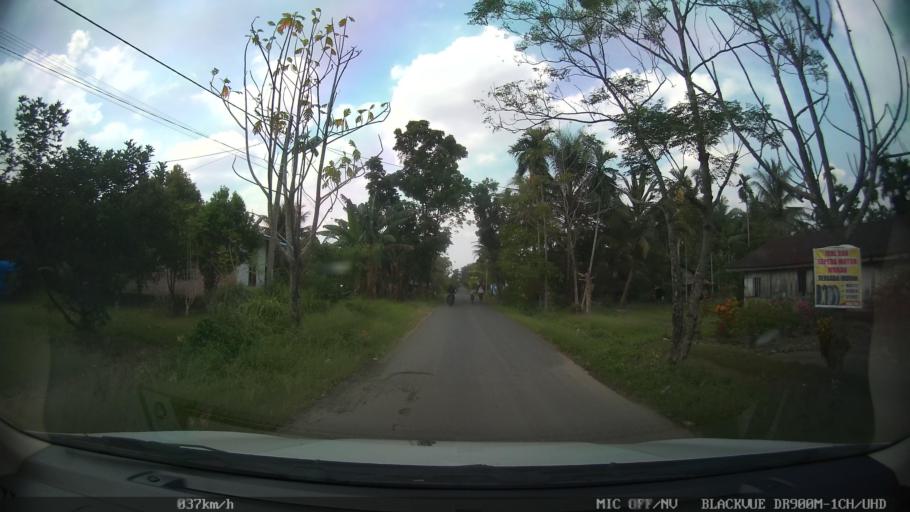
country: ID
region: North Sumatra
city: Binjai
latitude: 3.6314
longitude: 98.5173
